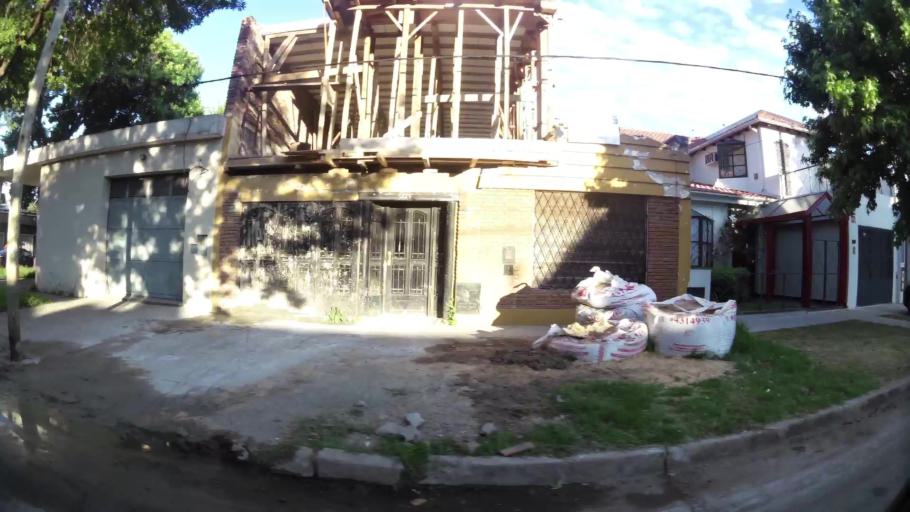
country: AR
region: Santa Fe
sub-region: Departamento de Rosario
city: Rosario
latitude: -32.9717
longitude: -60.6659
